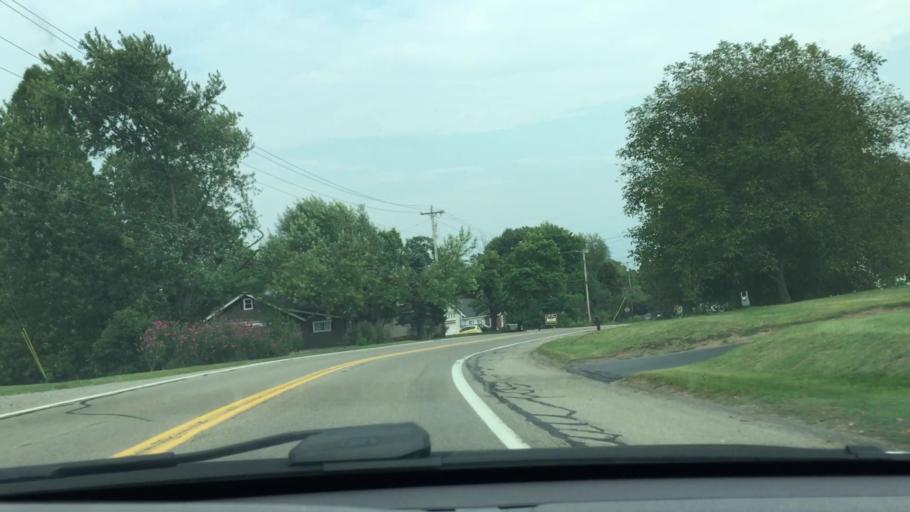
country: US
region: Pennsylvania
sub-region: Lawrence County
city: Oakland
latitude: 40.9698
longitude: -80.4077
